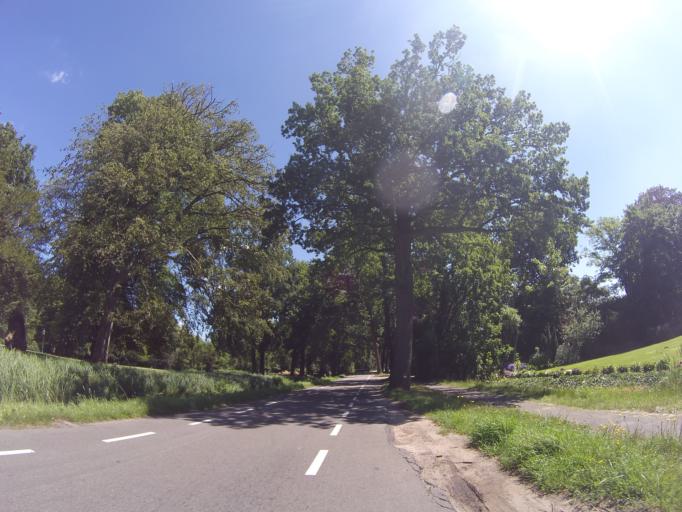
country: NL
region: Utrecht
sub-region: Gemeente De Bilt
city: De Bilt
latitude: 52.1228
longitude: 5.1541
